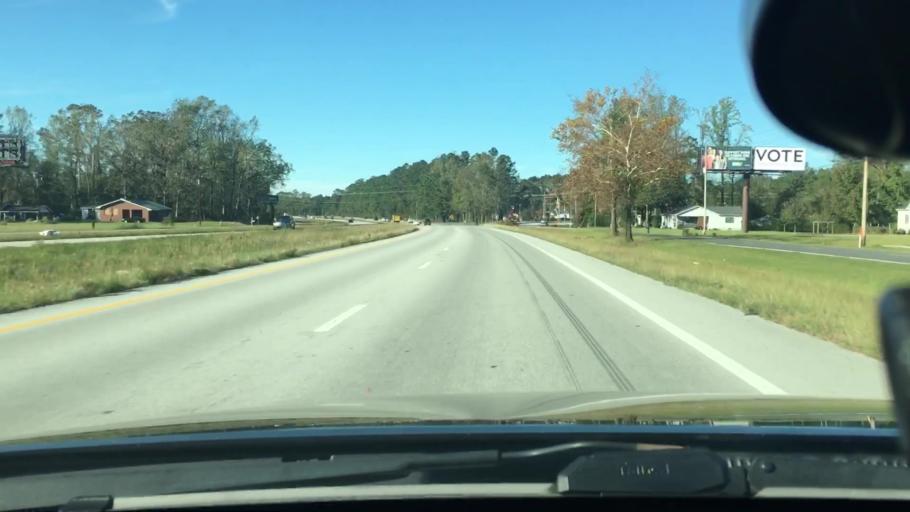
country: US
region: North Carolina
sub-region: Craven County
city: Neuse Forest
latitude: 34.9520
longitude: -76.9487
